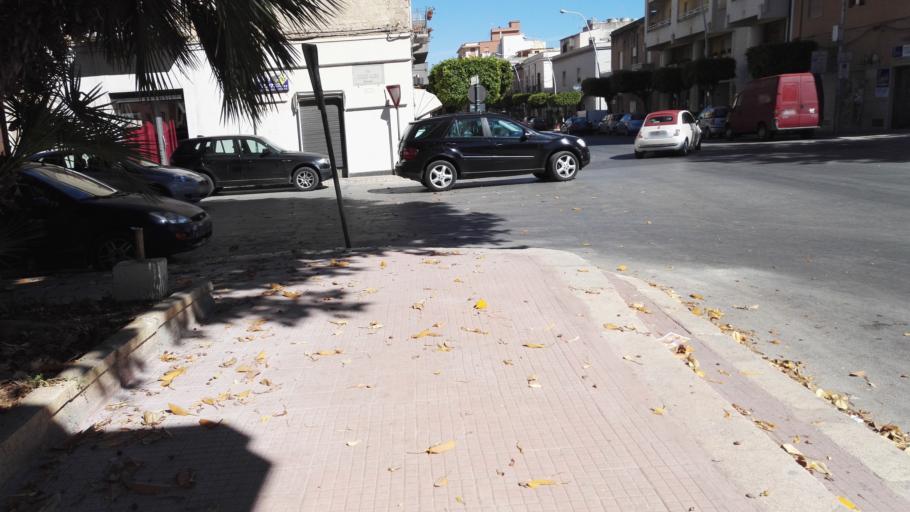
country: IT
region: Sicily
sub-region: Trapani
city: Marsala
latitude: 37.7964
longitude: 12.4354
